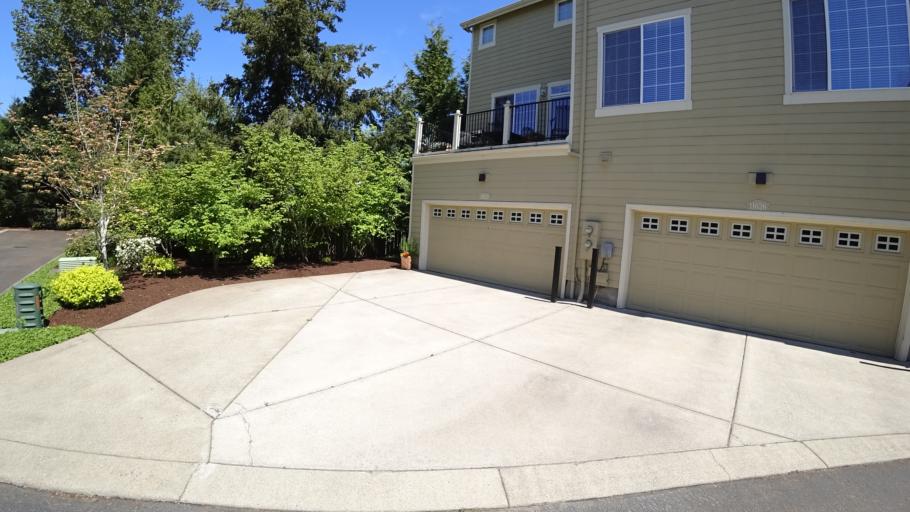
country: US
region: Oregon
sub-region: Washington County
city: King City
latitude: 45.4358
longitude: -122.8239
